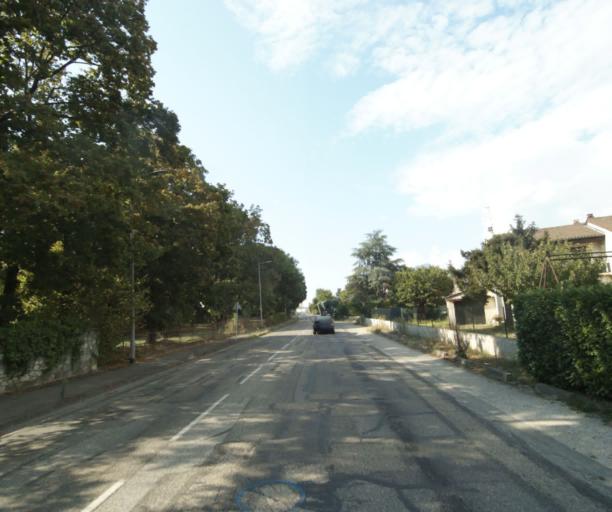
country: FR
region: Rhone-Alpes
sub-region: Departement de l'Isere
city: Echirolles
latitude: 45.1440
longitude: 5.7284
